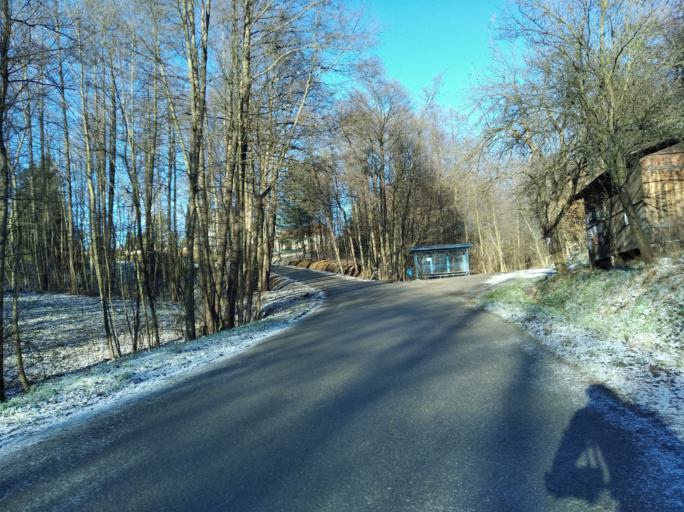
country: PL
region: Subcarpathian Voivodeship
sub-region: Powiat ropczycko-sedziszowski
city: Iwierzyce
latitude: 49.9664
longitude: 21.7536
